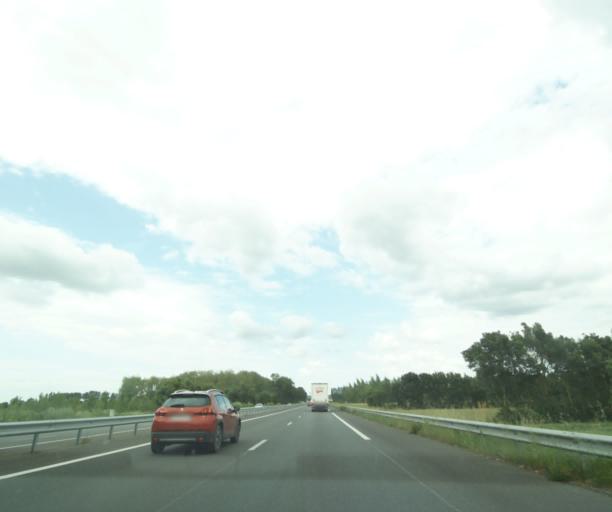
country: FR
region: Pays de la Loire
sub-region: Departement de Maine-et-Loire
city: Vivy
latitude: 47.2975
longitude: -0.0395
